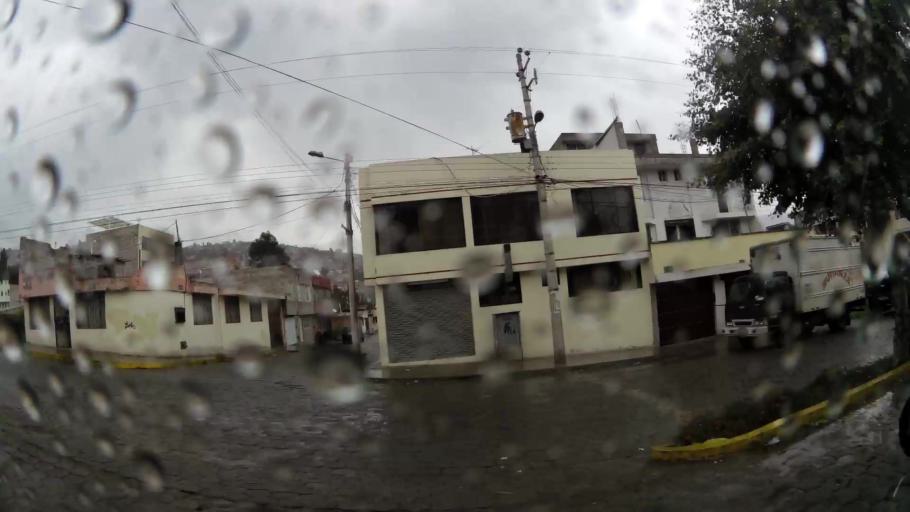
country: EC
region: Pichincha
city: Quito
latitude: -0.0971
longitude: -78.5001
